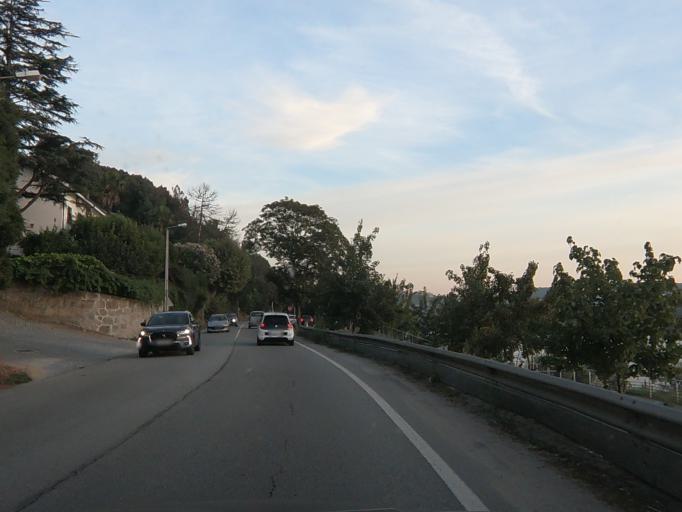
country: PT
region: Porto
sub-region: Gondomar
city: Valbom
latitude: 41.1327
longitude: -8.5694
